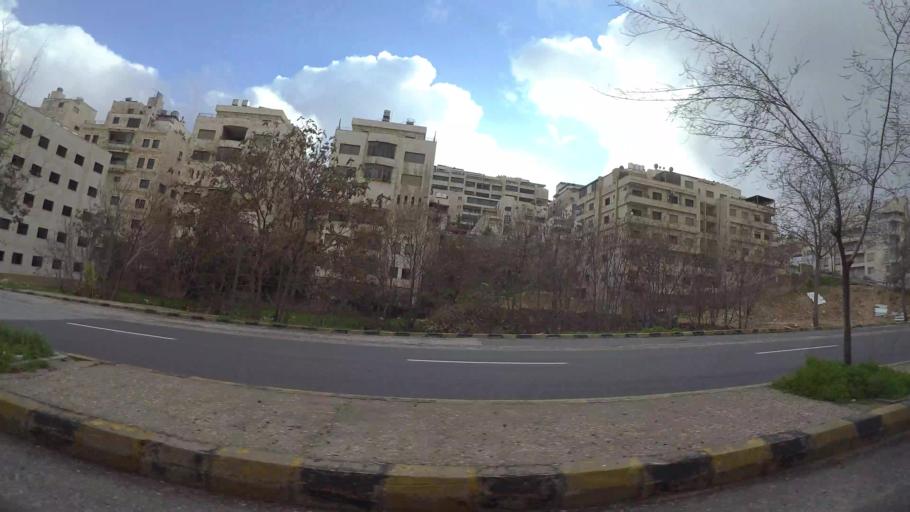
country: JO
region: Amman
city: Al Bunayyat ash Shamaliyah
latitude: 31.9430
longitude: 35.8932
